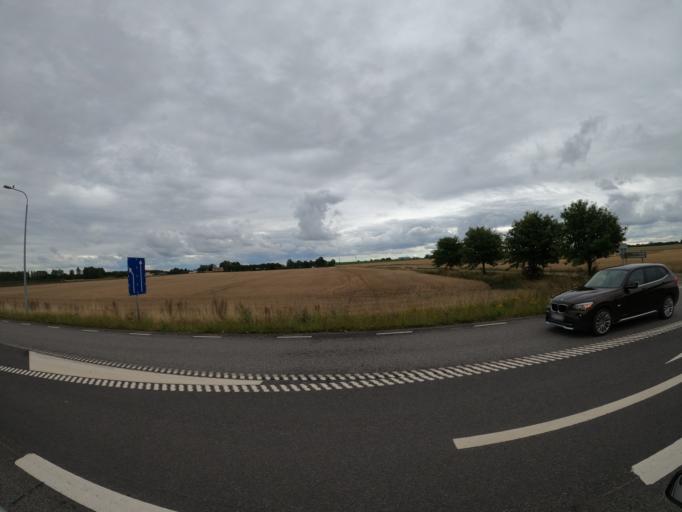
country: SE
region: Skane
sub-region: Lunds Kommun
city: Lund
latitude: 55.7431
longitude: 13.1992
